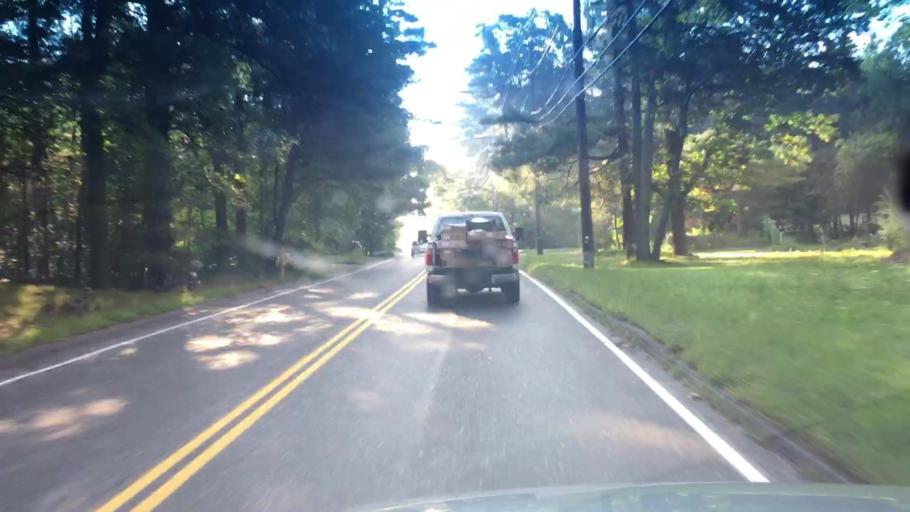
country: US
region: Massachusetts
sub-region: Norfolk County
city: Medfield
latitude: 42.1680
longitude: -71.2909
